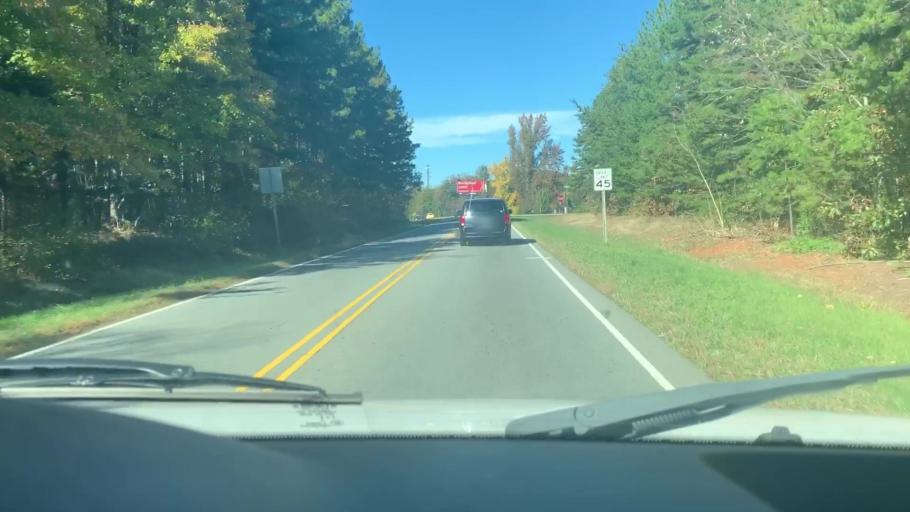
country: US
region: North Carolina
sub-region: Lincoln County
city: Lowesville
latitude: 35.4401
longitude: -80.9803
